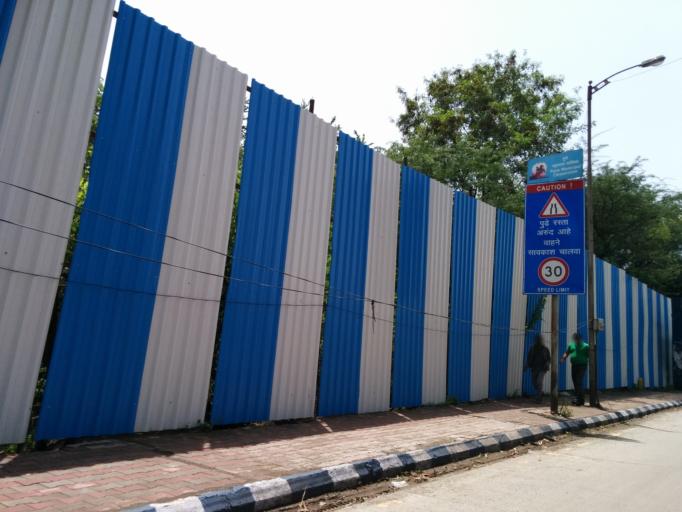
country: IN
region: Maharashtra
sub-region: Pune Division
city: Pune
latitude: 18.5336
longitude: 73.9151
